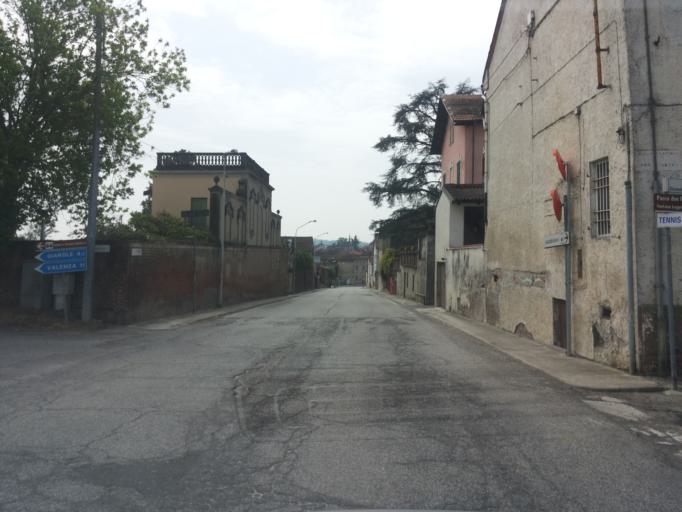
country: IT
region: Piedmont
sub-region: Provincia di Alessandria
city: Mirabello Monferrato
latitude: 45.0382
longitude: 8.5254
